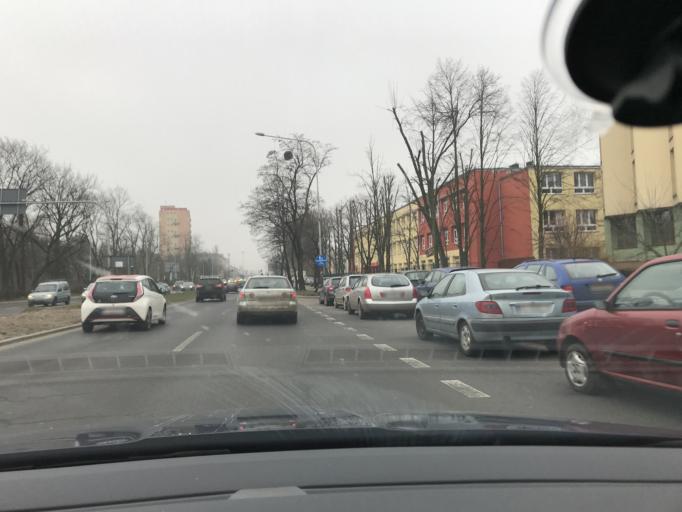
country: PL
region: Lodz Voivodeship
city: Lodz
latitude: 51.7780
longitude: 19.4815
